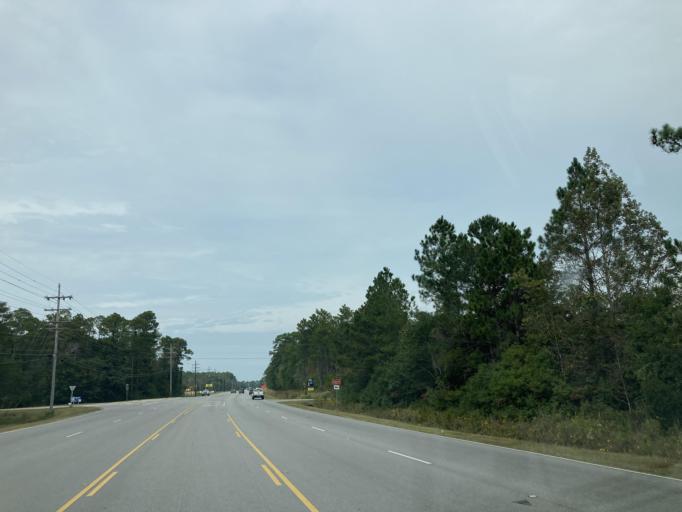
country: US
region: Mississippi
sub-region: Jackson County
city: Gulf Hills
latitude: 30.4641
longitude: -88.8462
